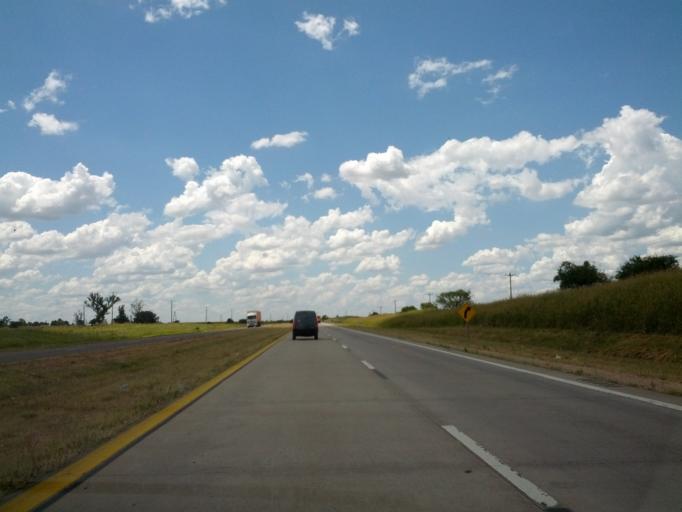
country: AR
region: Entre Rios
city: Gualeguaychu
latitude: -32.9215
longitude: -58.5671
